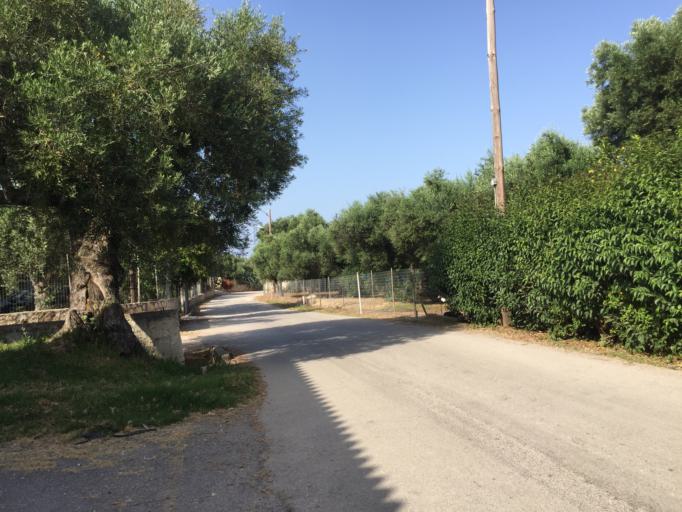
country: GR
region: Ionian Islands
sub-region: Nomos Zakynthou
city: Vanaton
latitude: 37.8234
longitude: 20.8558
